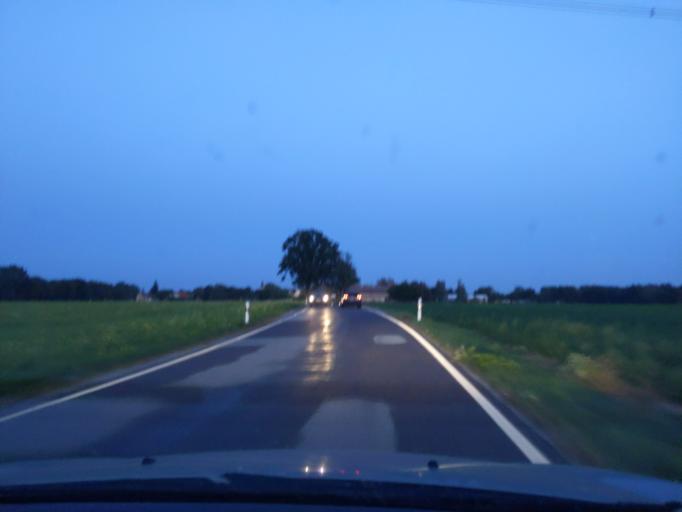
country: DE
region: Saxony
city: Grossdubrau
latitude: 51.2990
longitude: 14.4456
